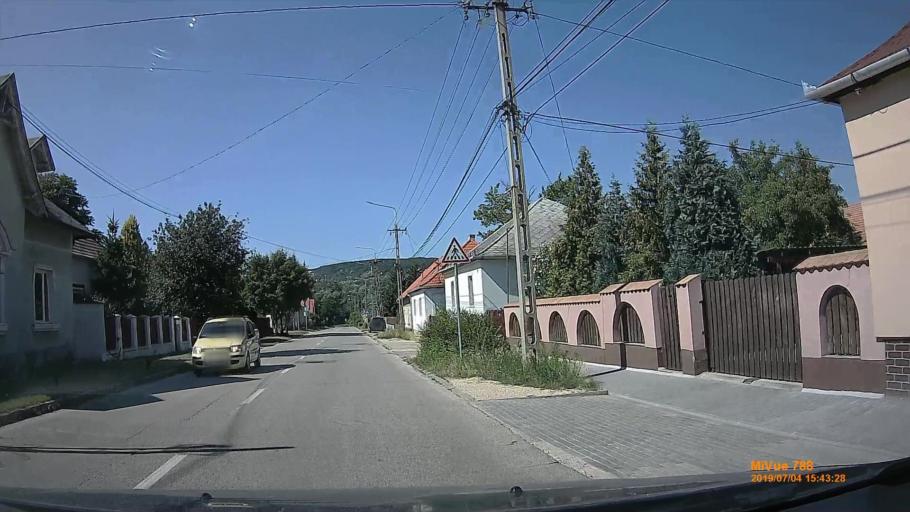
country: HU
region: Komarom-Esztergom
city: Tatabanya
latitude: 47.5658
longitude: 18.4174
